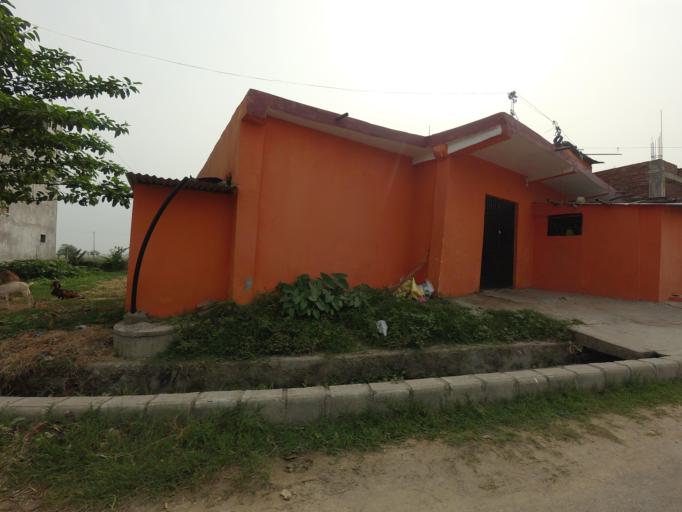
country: NP
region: Western Region
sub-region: Lumbini Zone
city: Bhairahawa
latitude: 27.4875
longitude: 83.4366
